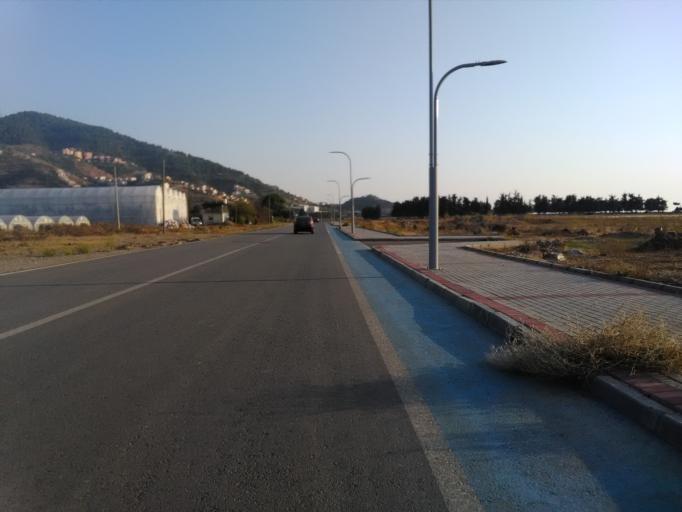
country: TR
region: Antalya
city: Gazipasa
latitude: 36.2480
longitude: 32.2945
